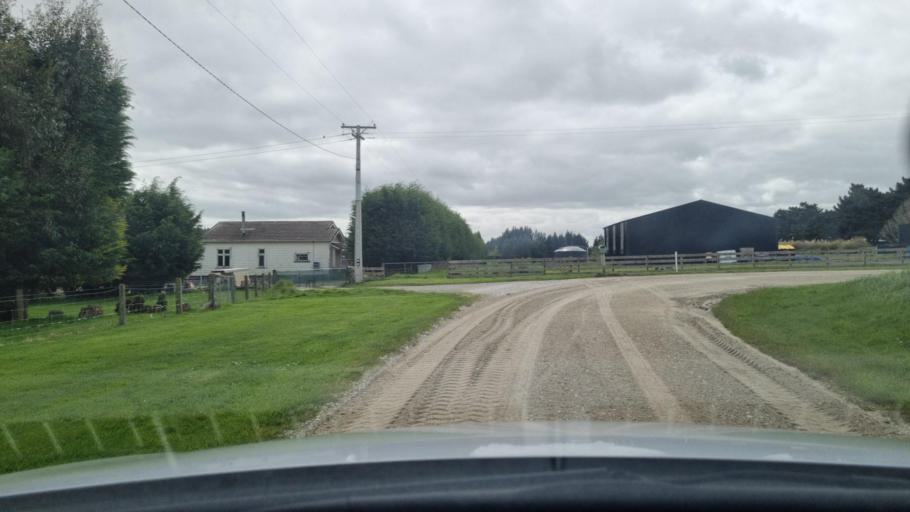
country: NZ
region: Southland
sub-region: Invercargill City
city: Invercargill
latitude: -46.4329
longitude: 168.4104
